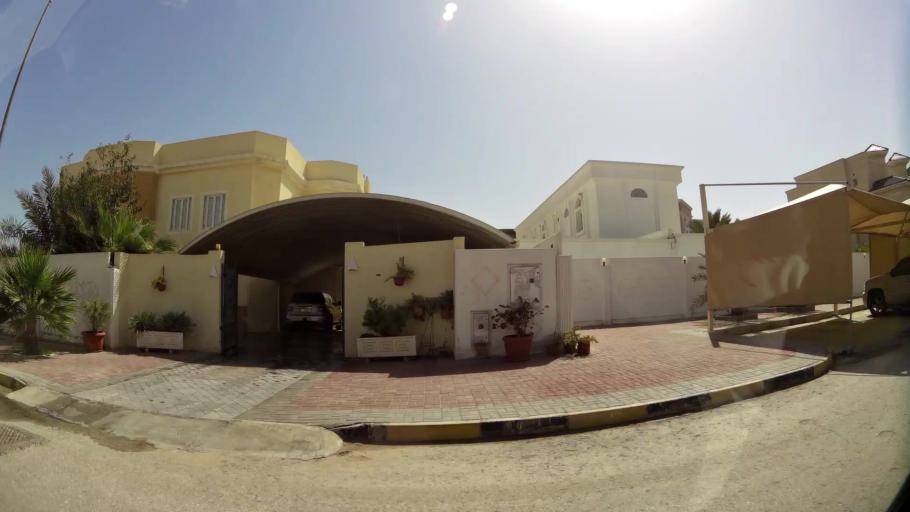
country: QA
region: Baladiyat ad Dawhah
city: Doha
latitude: 25.3585
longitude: 51.4960
